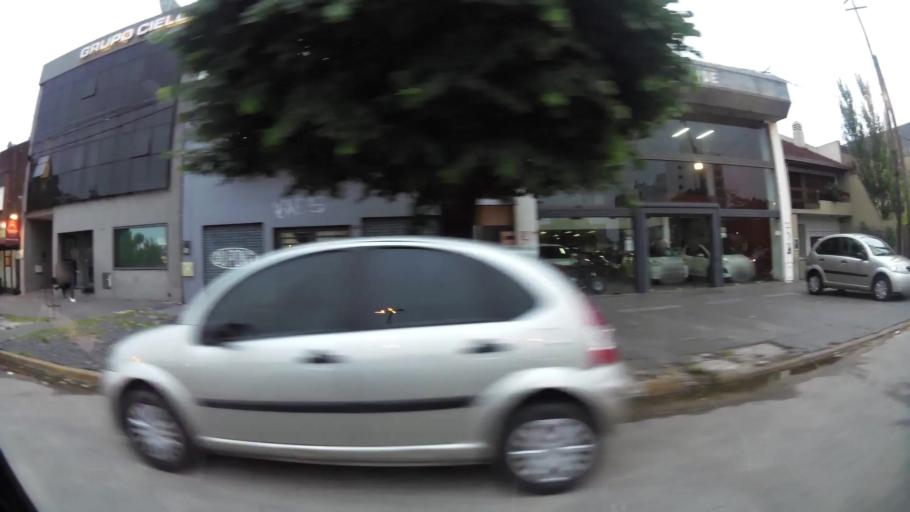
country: AR
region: Buenos Aires
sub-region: Partido de La Plata
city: La Plata
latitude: -34.9018
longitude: -57.9713
